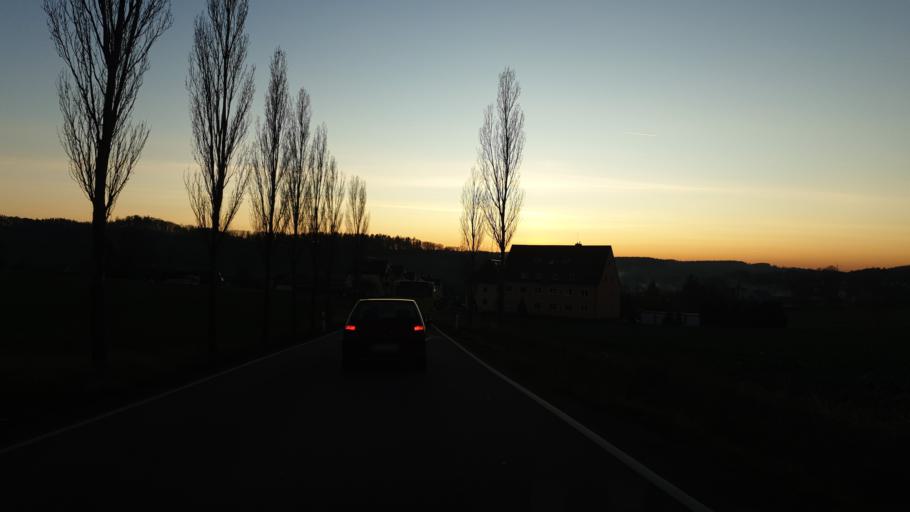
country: DE
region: Saxony
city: Hohndorf
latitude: 50.7489
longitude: 12.6738
